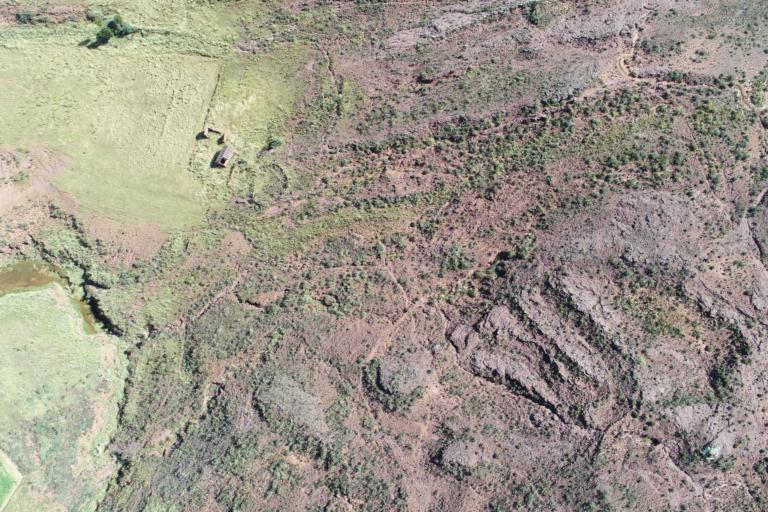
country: BO
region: La Paz
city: Tiahuanaco
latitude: -16.6018
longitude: -68.7587
